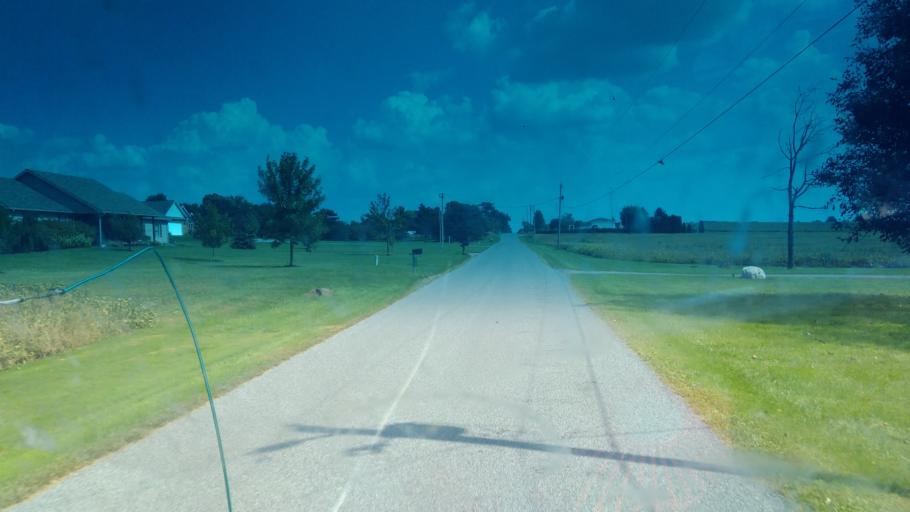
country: US
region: Ohio
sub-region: Hardin County
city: Ada
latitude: 40.7186
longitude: -83.8355
